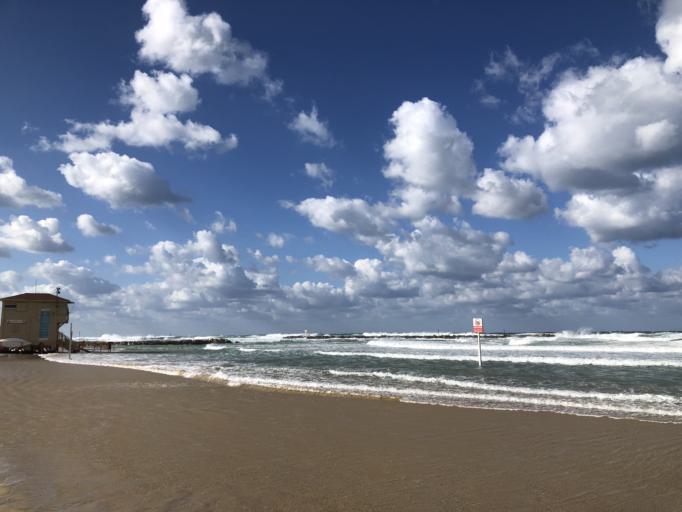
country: IL
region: Tel Aviv
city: Tel Aviv
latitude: 32.0784
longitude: 34.7660
